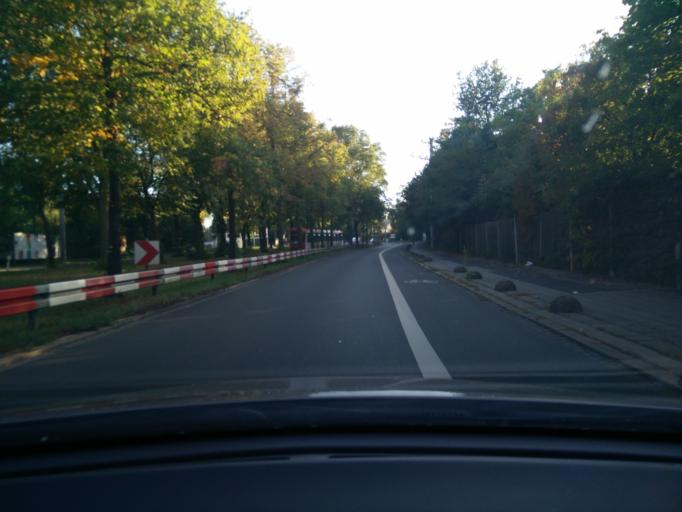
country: DE
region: Bavaria
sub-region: Regierungsbezirk Mittelfranken
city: Nuernberg
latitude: 49.4210
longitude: 11.0843
